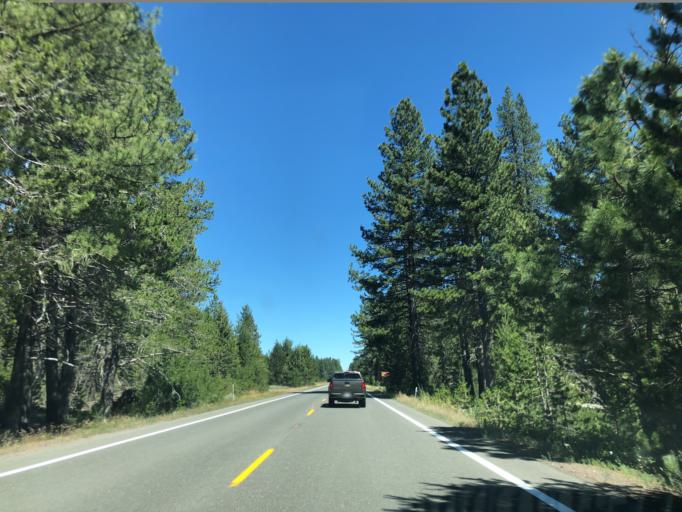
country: US
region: California
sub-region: Lassen County
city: Westwood
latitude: 40.4476
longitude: -120.8910
